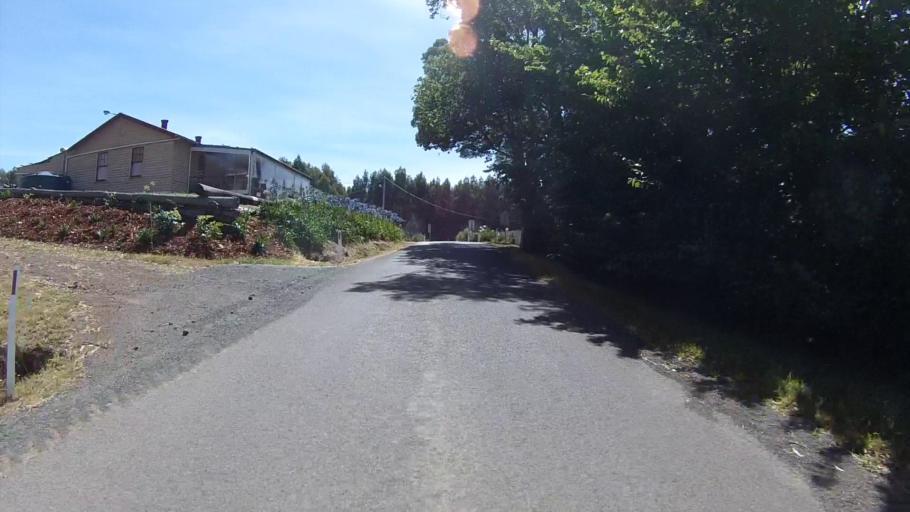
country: AU
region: Tasmania
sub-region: Sorell
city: Sorell
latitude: -42.7118
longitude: 147.7521
